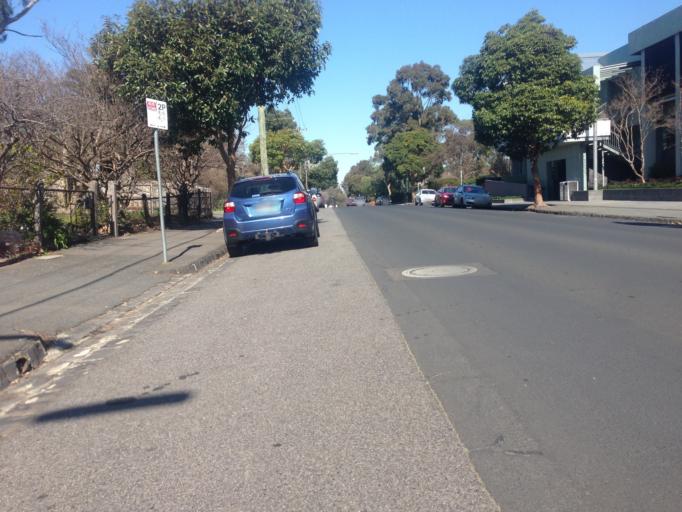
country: AU
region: Victoria
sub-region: Boroondara
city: Kew
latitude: -37.8078
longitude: 145.0354
